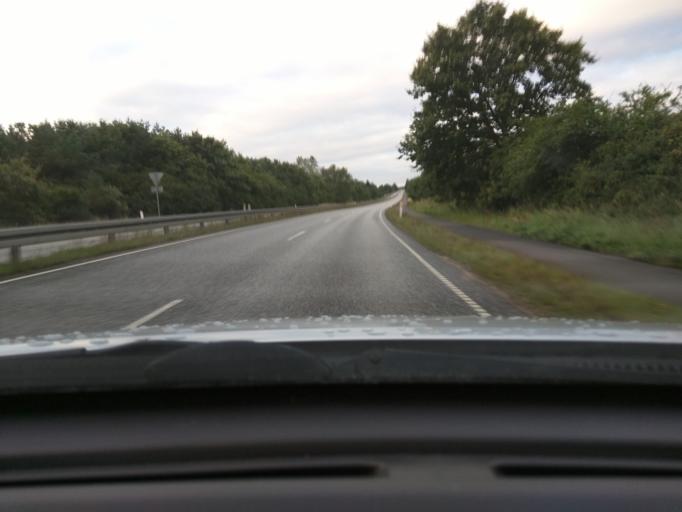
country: DK
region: Central Jutland
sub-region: Viborg Kommune
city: Viborg
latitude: 56.4246
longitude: 9.3887
